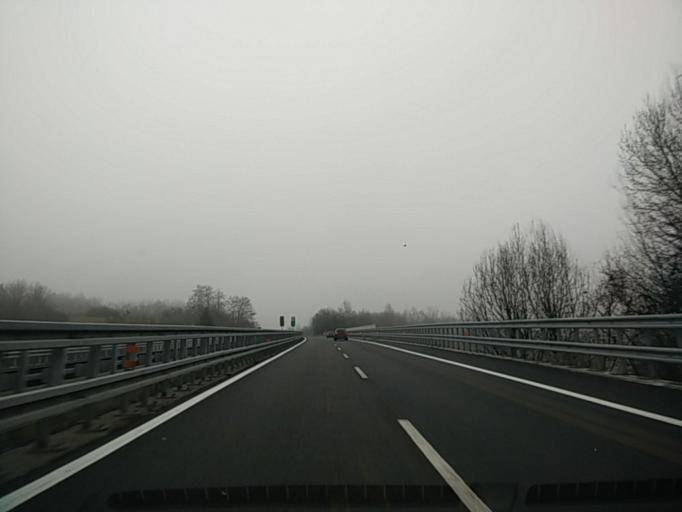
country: IT
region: Piedmont
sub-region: Provincia di Asti
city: Baldichieri d'Asti
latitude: 44.9014
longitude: 8.1308
